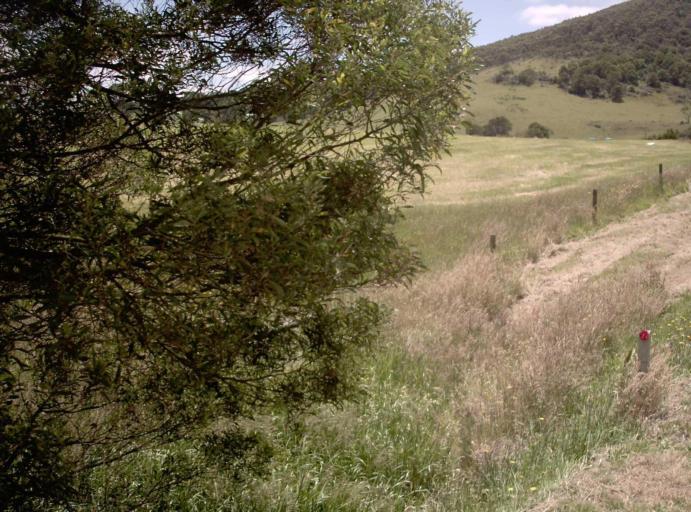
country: AU
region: Victoria
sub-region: Bass Coast
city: North Wonthaggi
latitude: -38.7165
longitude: 146.1110
